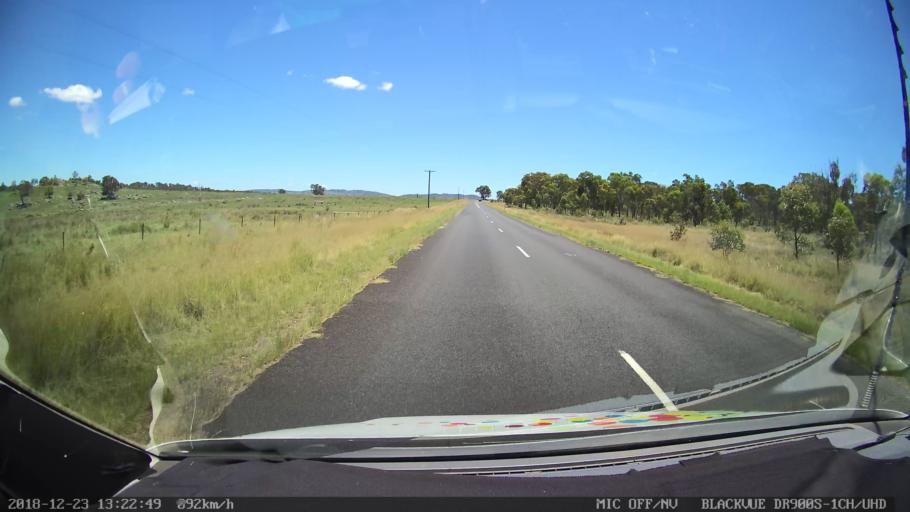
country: AU
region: New South Wales
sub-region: Armidale Dumaresq
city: Armidale
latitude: -30.4803
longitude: 151.4157
